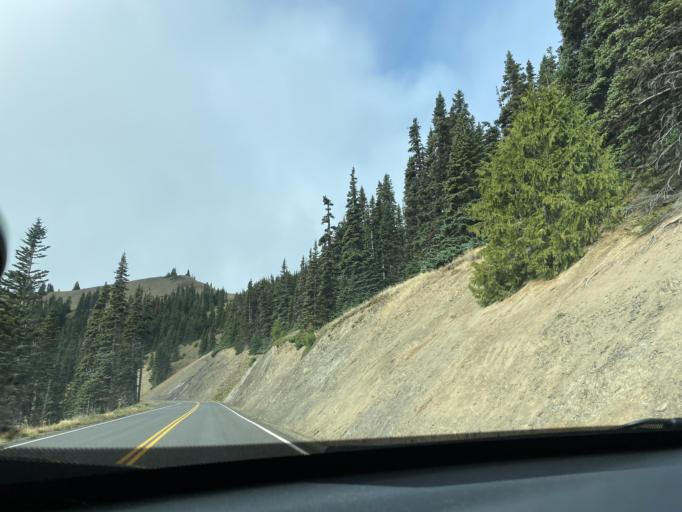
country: US
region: Washington
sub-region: Clallam County
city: Port Angeles
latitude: 47.9738
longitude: -123.4836
